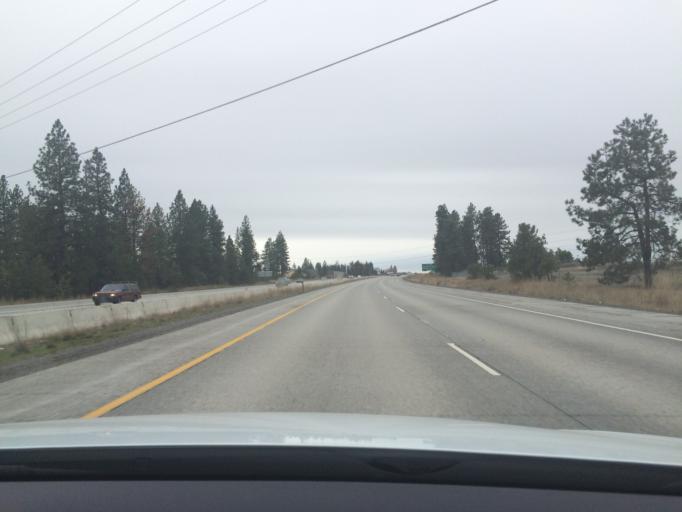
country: US
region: Washington
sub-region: Spokane County
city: Airway Heights
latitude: 47.6158
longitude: -117.5101
